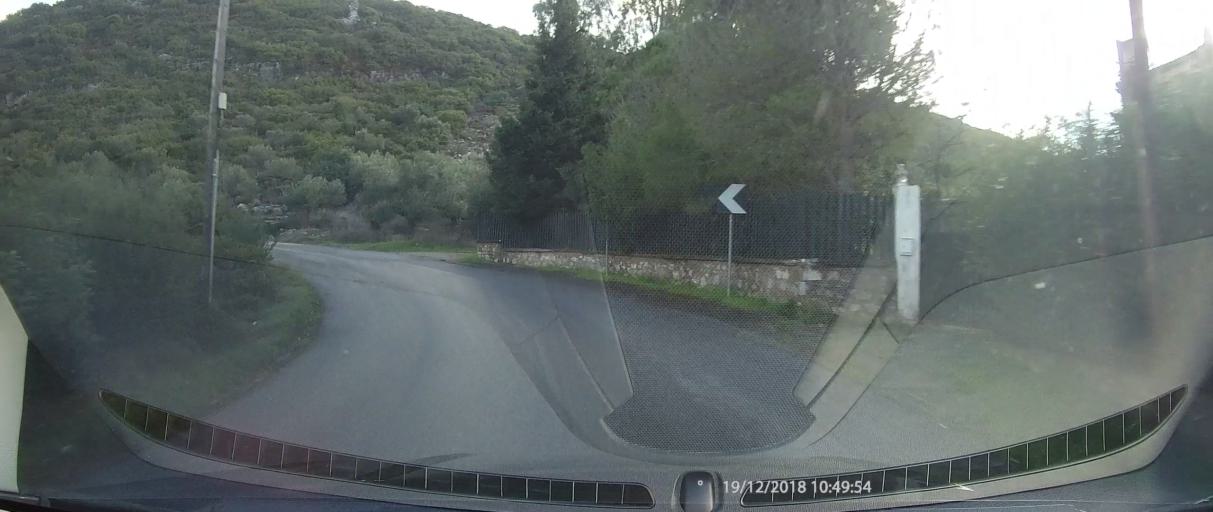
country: GR
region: Peloponnese
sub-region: Nomos Messinias
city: Kardamyli
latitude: 36.9225
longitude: 22.2029
